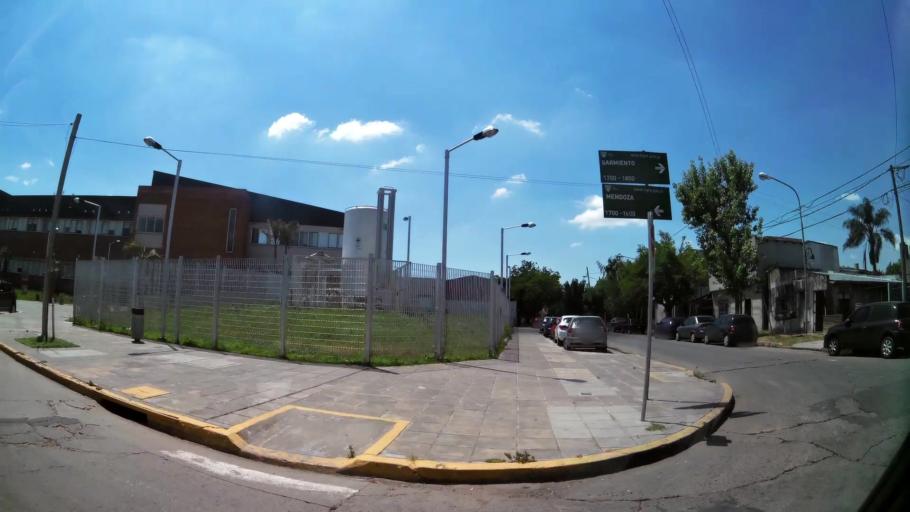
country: AR
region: Buenos Aires
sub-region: Partido de Tigre
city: Tigre
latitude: -34.4381
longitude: -58.5827
